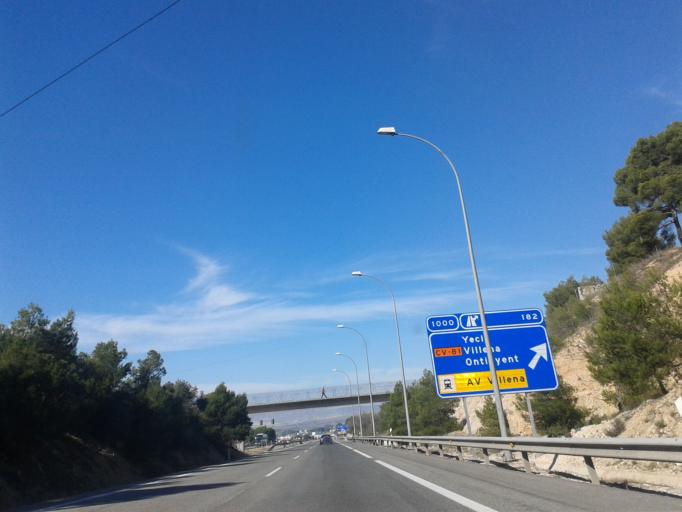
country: ES
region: Valencia
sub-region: Provincia de Alicante
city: Villena
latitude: 38.6376
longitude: -0.8588
